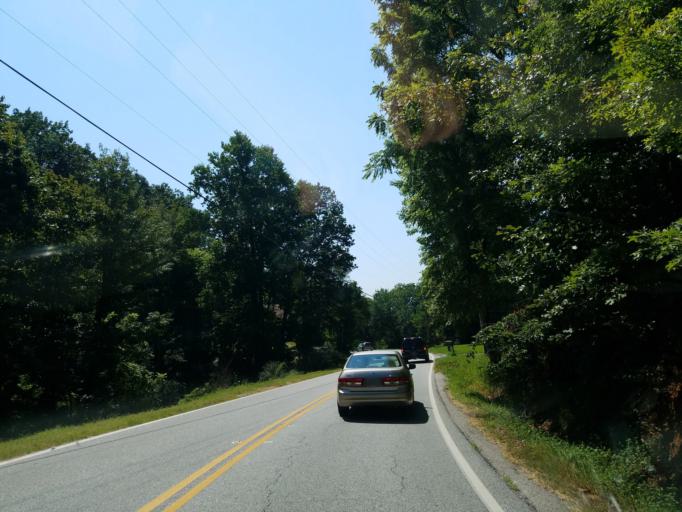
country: US
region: Georgia
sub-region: Lumpkin County
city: Dahlonega
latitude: 34.6099
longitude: -83.9692
